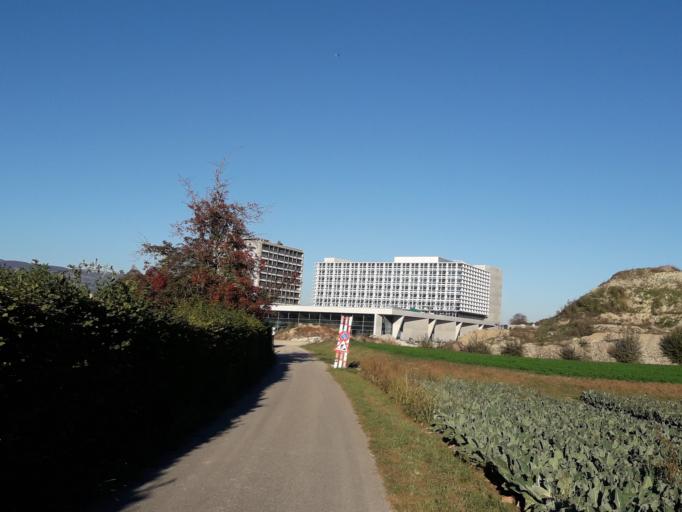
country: CH
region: Solothurn
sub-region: Bezirk Solothurn
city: Solothurn
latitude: 47.1968
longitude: 7.5363
